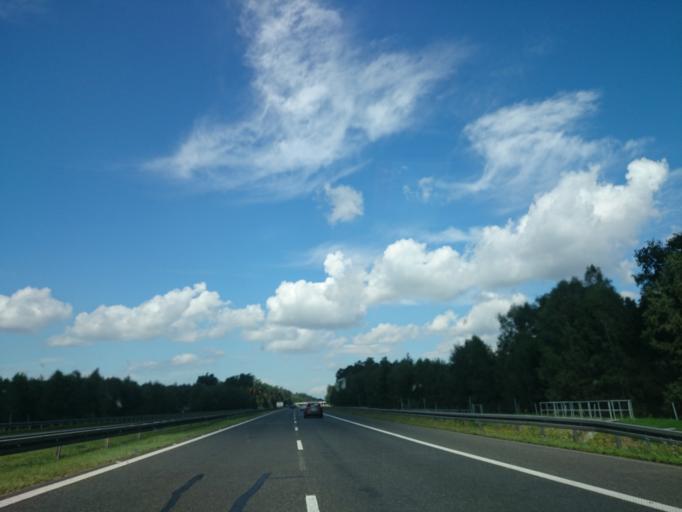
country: PL
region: Opole Voivodeship
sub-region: Powiat opolski
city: Niemodlin
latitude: 50.6669
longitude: 17.6794
